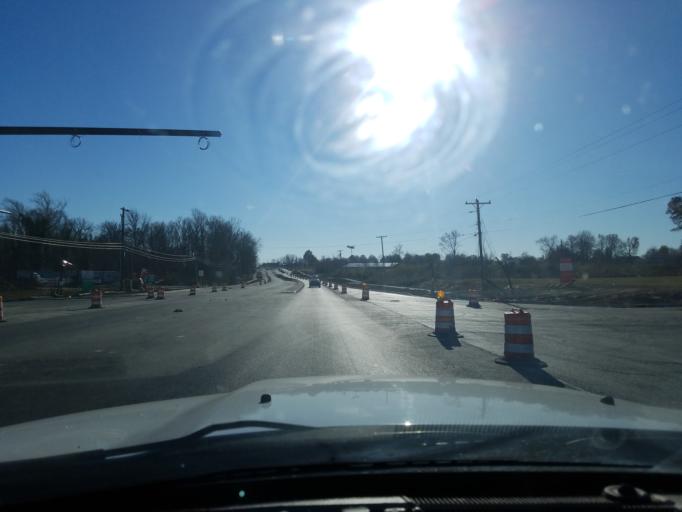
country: US
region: Indiana
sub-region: Clark County
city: Oak Park
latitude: 38.3329
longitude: -85.7096
